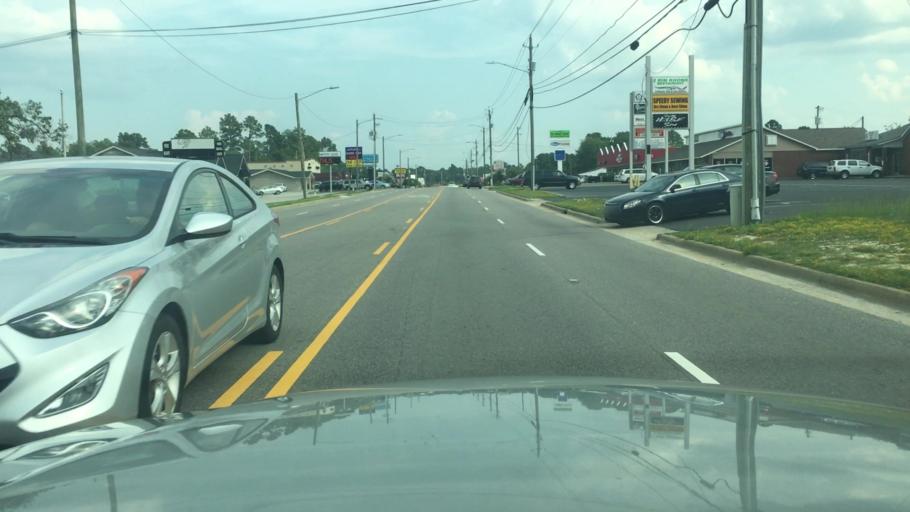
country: US
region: North Carolina
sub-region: Cumberland County
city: Fort Bragg
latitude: 35.1045
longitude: -78.9941
